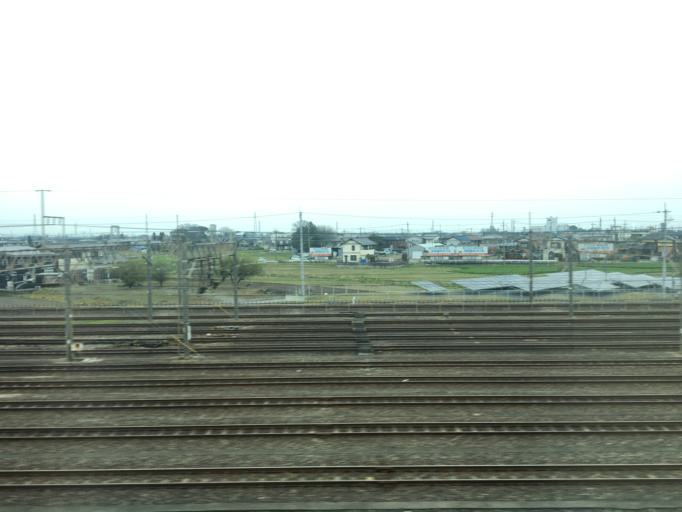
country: JP
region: Saitama
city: Kumagaya
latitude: 36.1598
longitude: 139.3573
